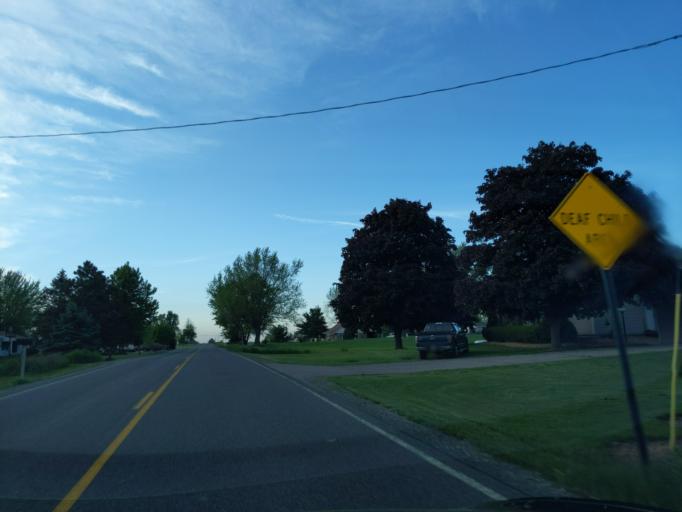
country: US
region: Michigan
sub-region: Ingham County
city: Williamston
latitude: 42.5825
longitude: -84.2985
